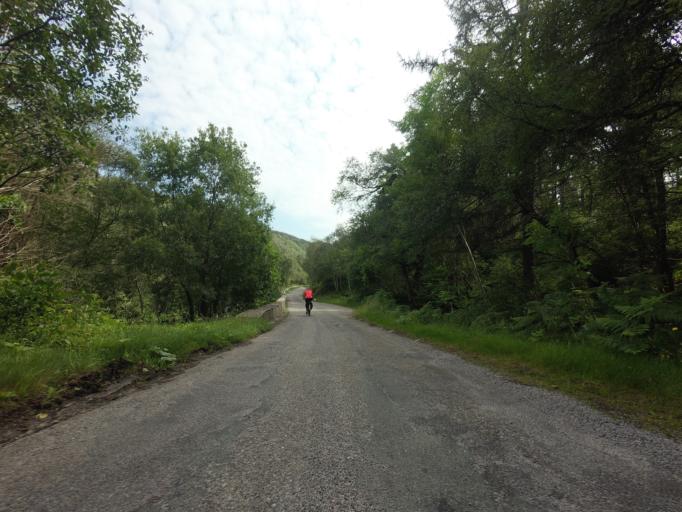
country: GB
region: Scotland
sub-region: Highland
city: Evanton
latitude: 57.9520
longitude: -4.4067
